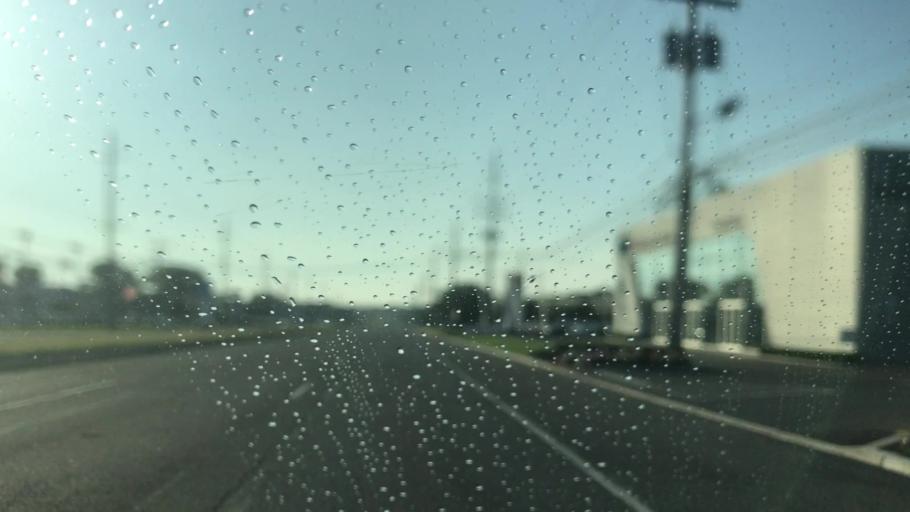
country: US
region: New Jersey
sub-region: Ocean County
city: Pine Beach
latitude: 39.9593
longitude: -74.1748
